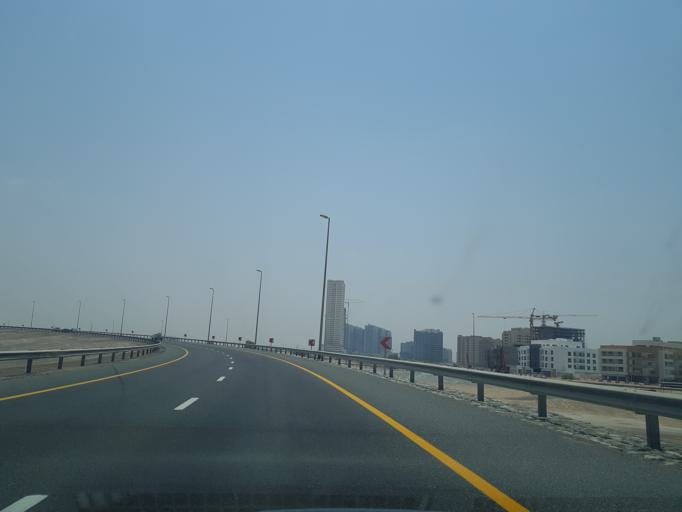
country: AE
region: Dubai
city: Dubai
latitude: 25.1022
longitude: 55.3761
